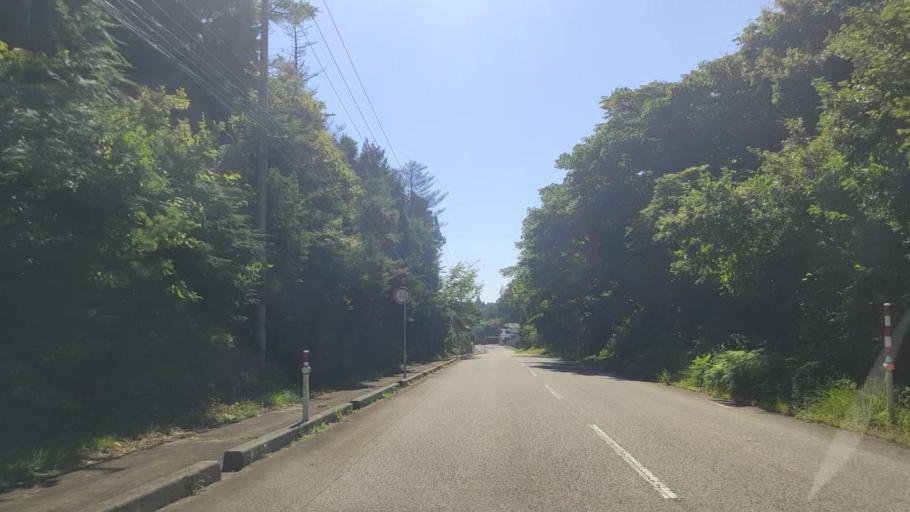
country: JP
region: Ishikawa
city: Nanao
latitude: 37.4689
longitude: 137.3236
